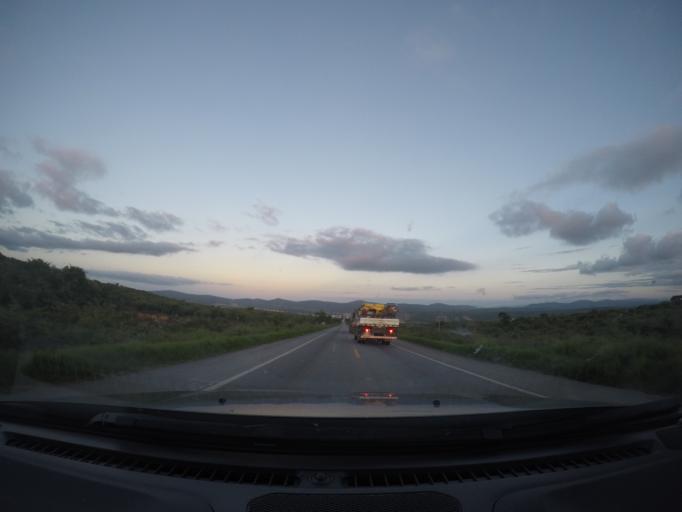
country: BR
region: Bahia
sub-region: Seabra
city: Seabra
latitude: -12.4319
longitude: -41.8042
